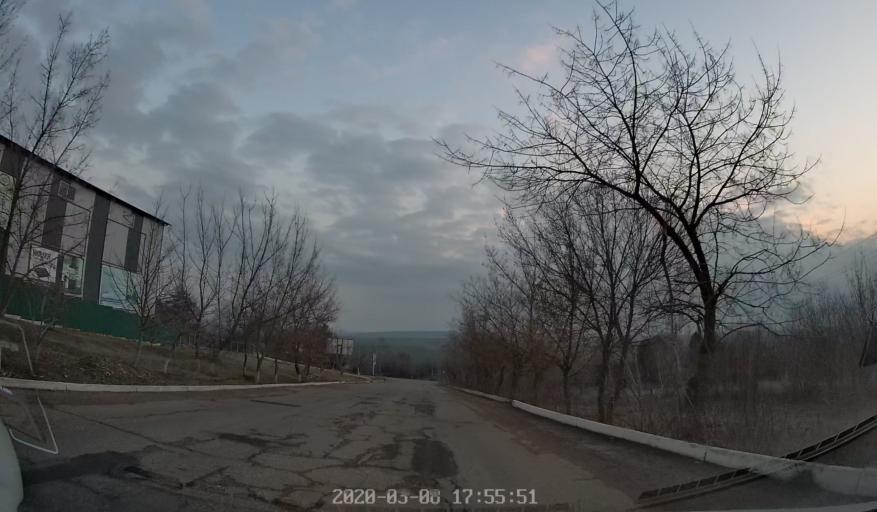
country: MD
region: Rezina
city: Rezina
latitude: 47.7500
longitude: 28.9490
